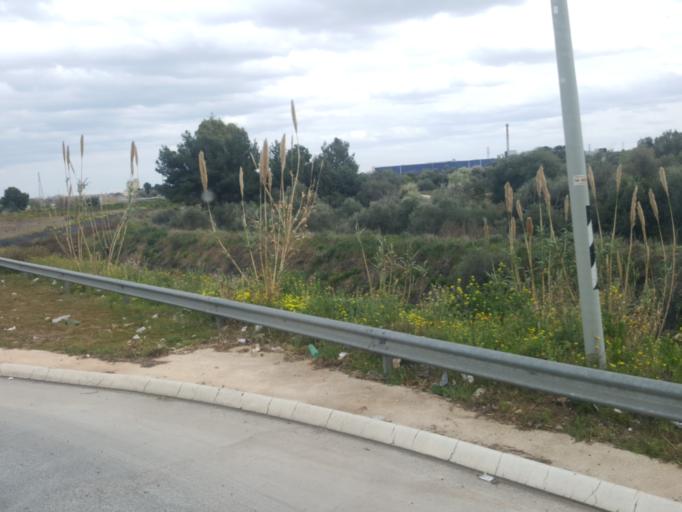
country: IT
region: Apulia
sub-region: Provincia di Bari
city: Modugno
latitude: 41.0973
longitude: 16.7824
